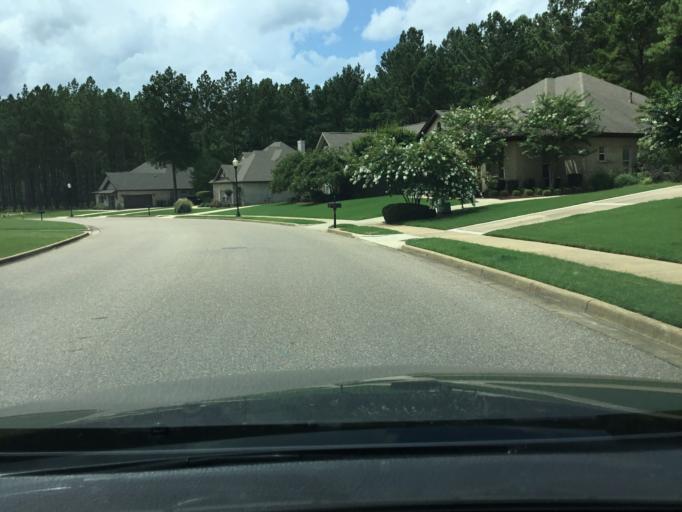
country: US
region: Alabama
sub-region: Montgomery County
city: Pike Road
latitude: 32.3443
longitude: -86.0803
